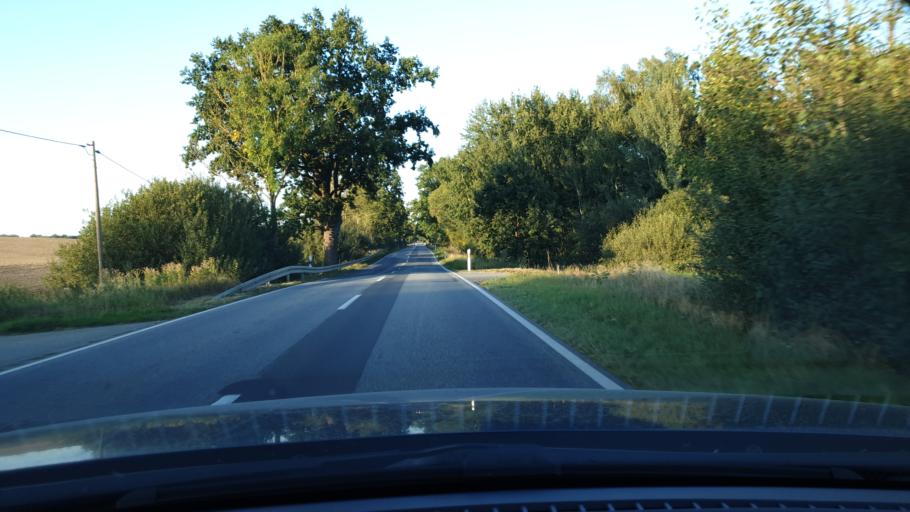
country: DE
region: Mecklenburg-Vorpommern
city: Lutzow
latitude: 53.6056
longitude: 11.1375
